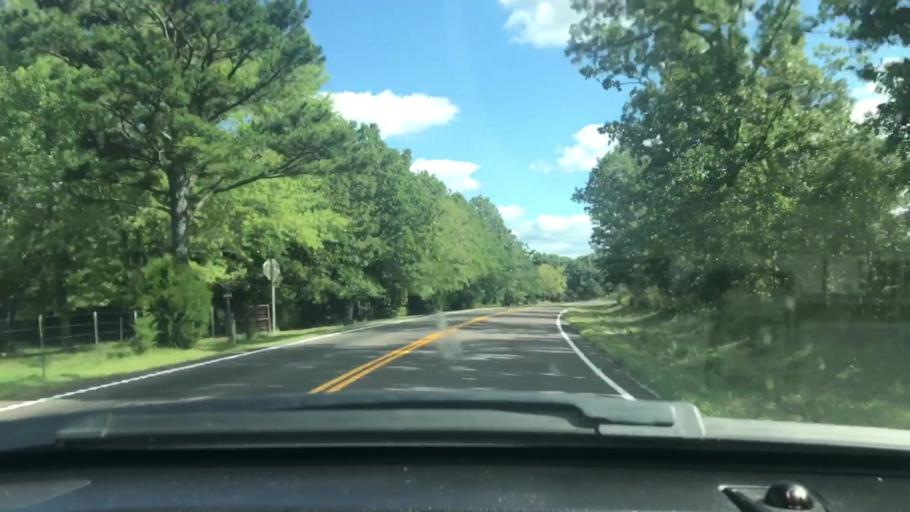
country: US
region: Missouri
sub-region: Wright County
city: Mountain Grove
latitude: 37.2301
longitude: -92.2940
